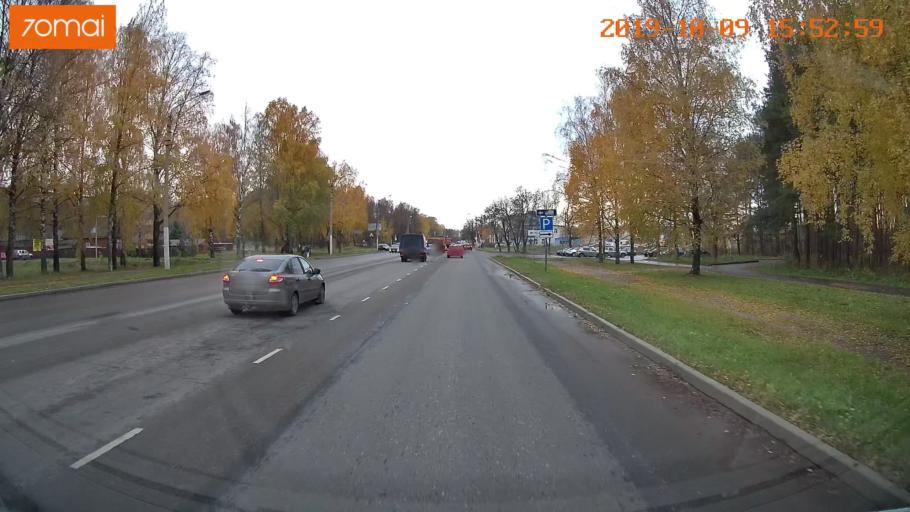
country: RU
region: Kostroma
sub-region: Kostromskoy Rayon
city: Kostroma
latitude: 57.7856
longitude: 40.9621
